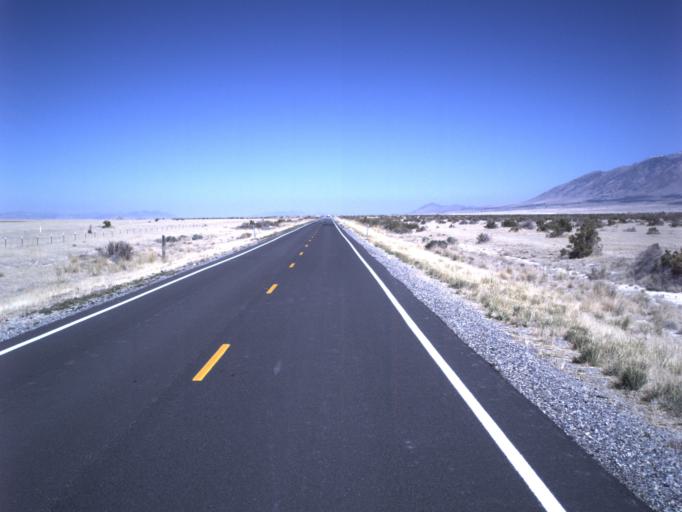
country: US
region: Utah
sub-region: Tooele County
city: Grantsville
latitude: 40.2655
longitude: -112.7410
